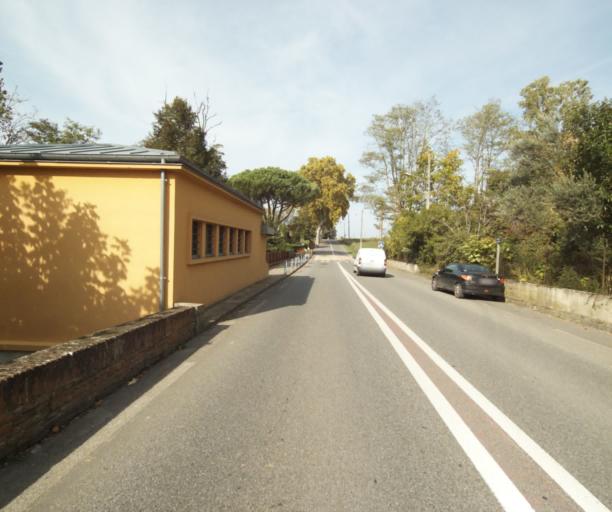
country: FR
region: Midi-Pyrenees
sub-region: Departement du Tarn-et-Garonne
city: Corbarieu
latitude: 43.9457
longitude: 1.3668
